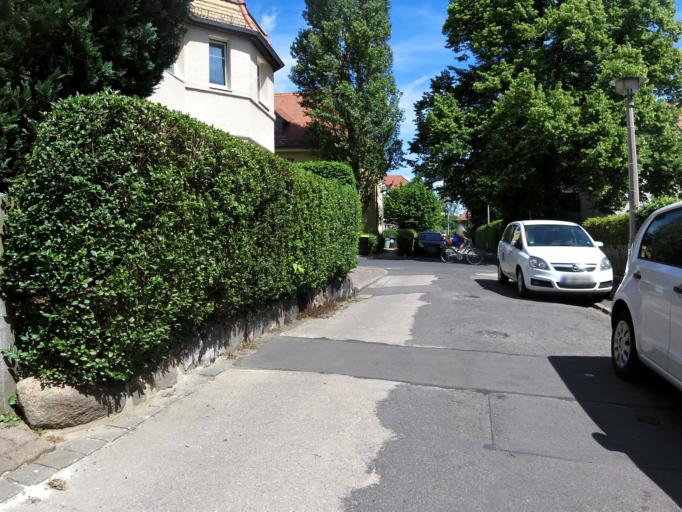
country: DE
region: Saxony
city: Leipzig
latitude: 51.3093
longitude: 12.4000
